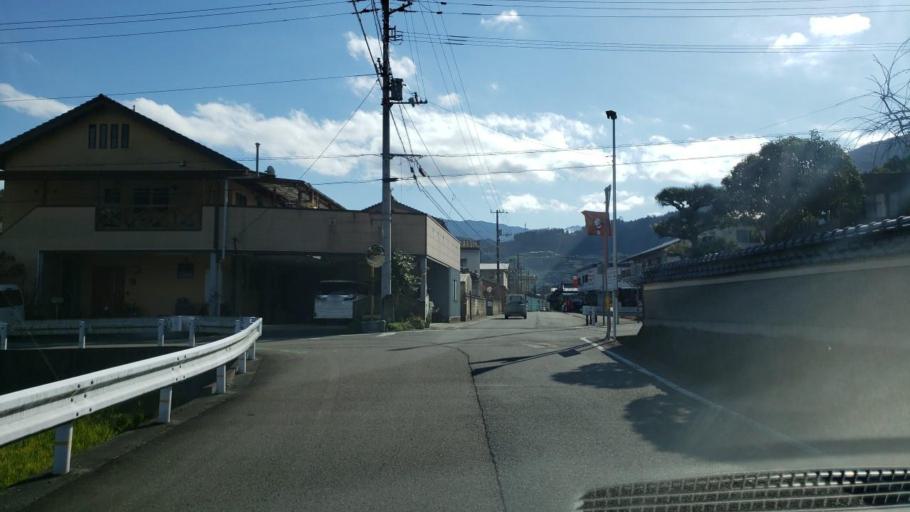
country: JP
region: Tokushima
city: Wakimachi
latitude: 34.0340
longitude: 134.0290
